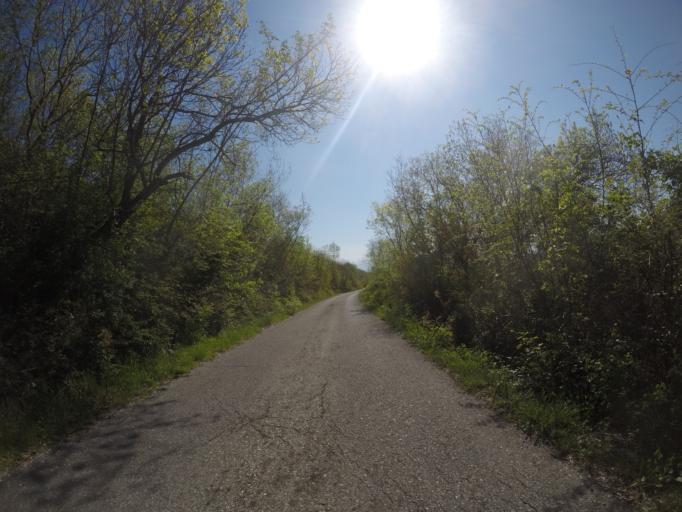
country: ME
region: Danilovgrad
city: Danilovgrad
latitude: 42.5138
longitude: 19.0683
